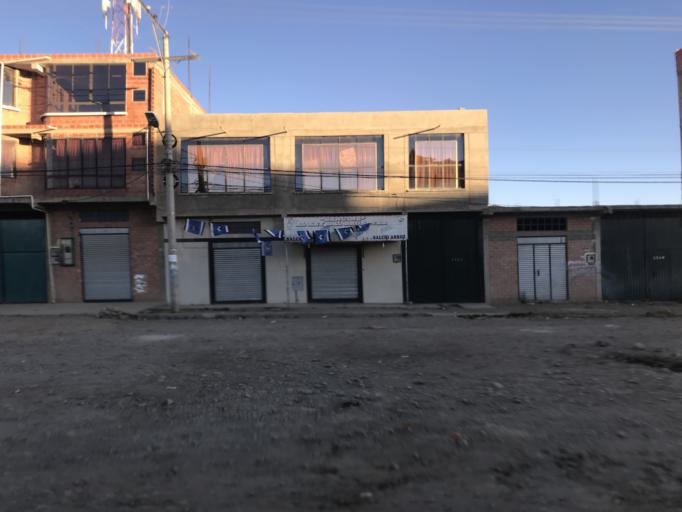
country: BO
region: La Paz
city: La Paz
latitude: -16.5034
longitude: -68.2464
